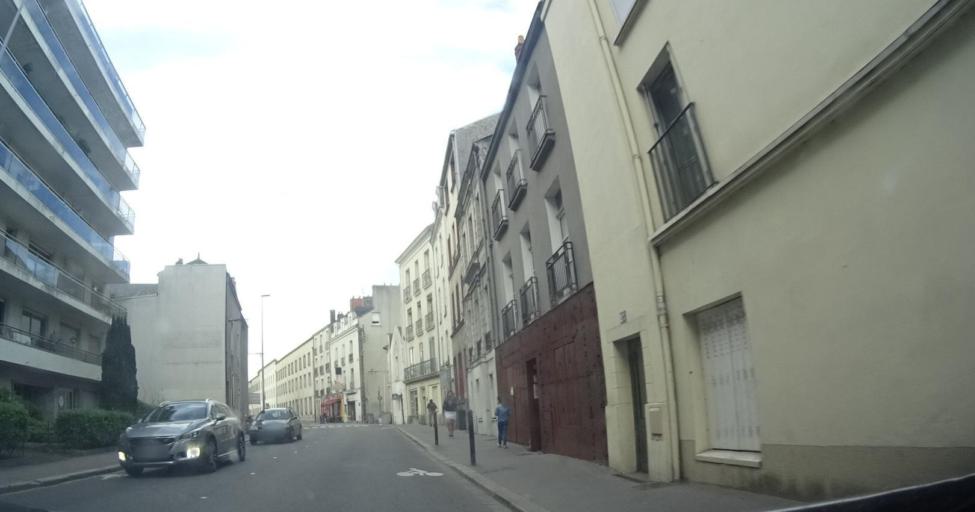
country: FR
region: Pays de la Loire
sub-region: Departement de la Loire-Atlantique
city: Nantes
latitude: 47.2224
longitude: -1.5465
